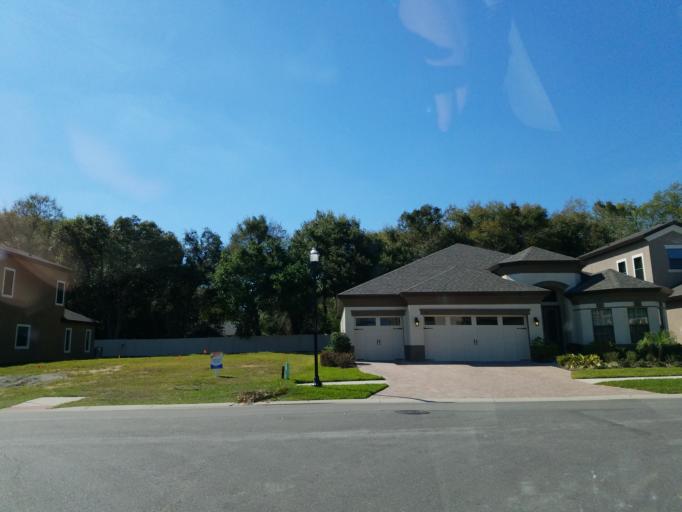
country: US
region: Florida
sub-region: Hillsborough County
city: Brandon
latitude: 27.9272
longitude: -82.2687
